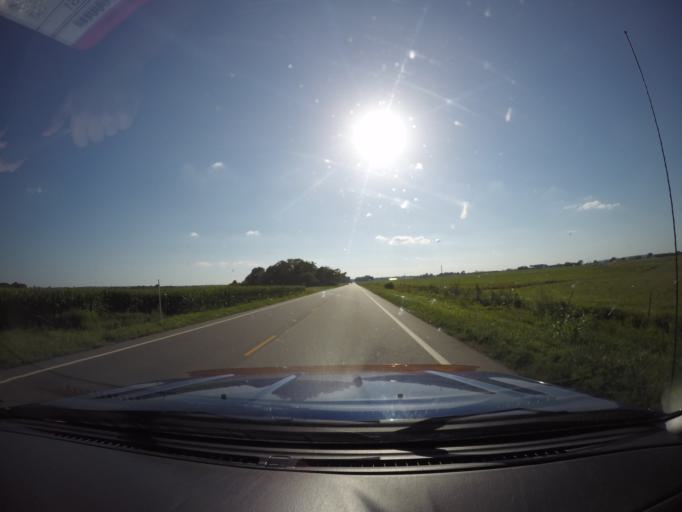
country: US
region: Kansas
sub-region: Douglas County
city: Lawrence
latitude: 39.0006
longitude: -95.2091
